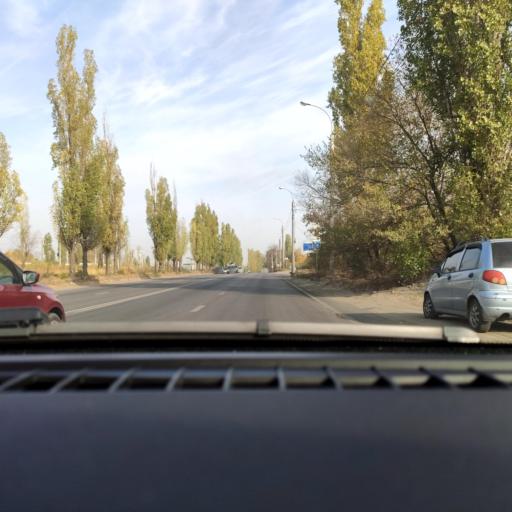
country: RU
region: Voronezj
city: Maslovka
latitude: 51.6153
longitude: 39.2582
